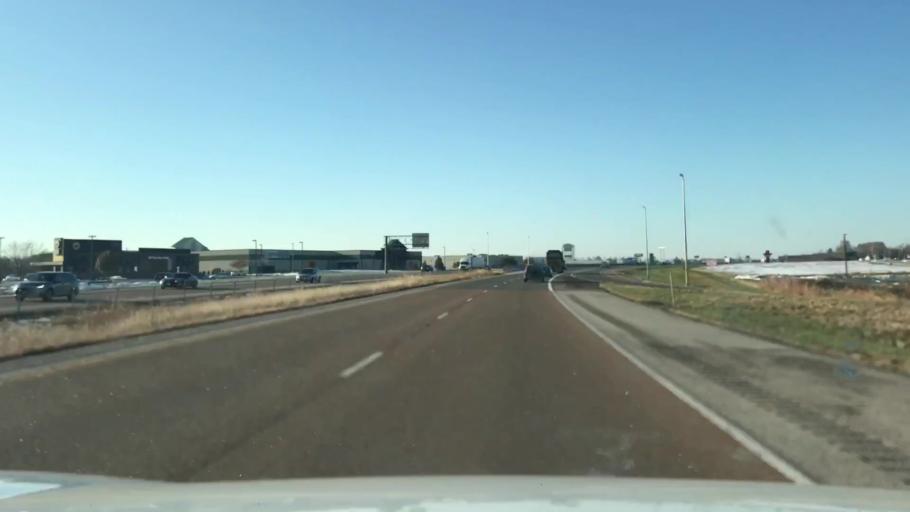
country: US
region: Illinois
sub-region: Saint Clair County
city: O'Fallon
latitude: 38.5775
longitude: -89.9316
